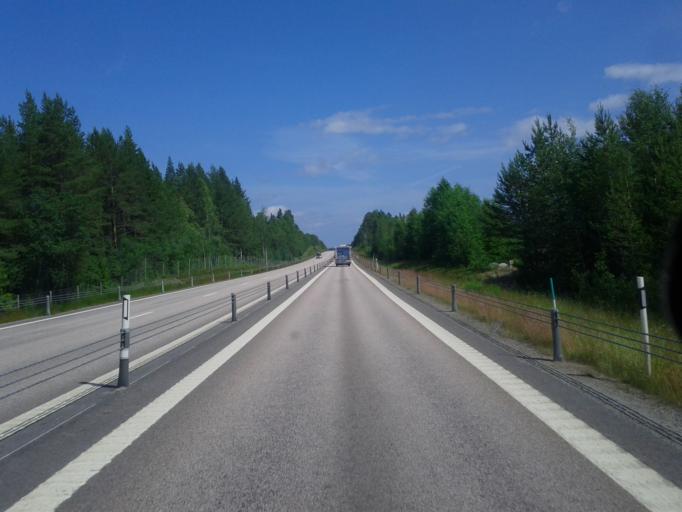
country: SE
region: Vaesterbotten
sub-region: Nordmalings Kommun
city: Nordmaling
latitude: 63.5164
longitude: 19.3672
